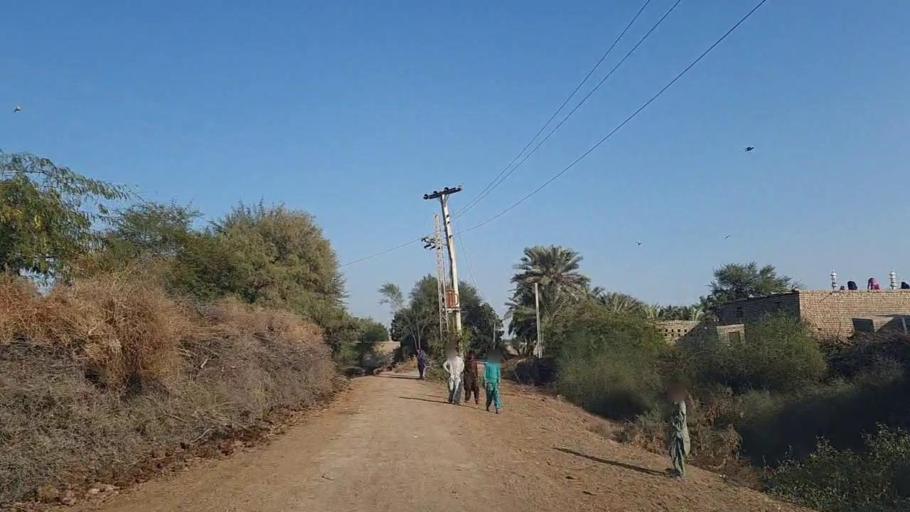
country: PK
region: Sindh
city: Shahpur Chakar
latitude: 26.2019
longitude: 68.6526
